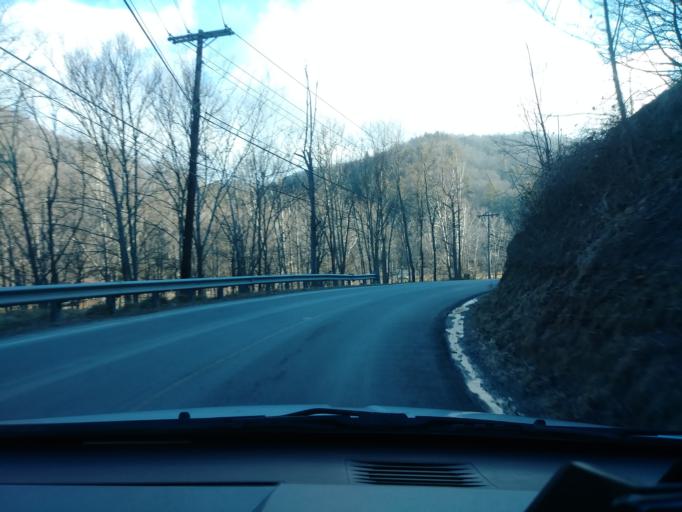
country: US
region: North Carolina
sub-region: Avery County
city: Banner Elk
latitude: 36.1727
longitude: -81.9471
